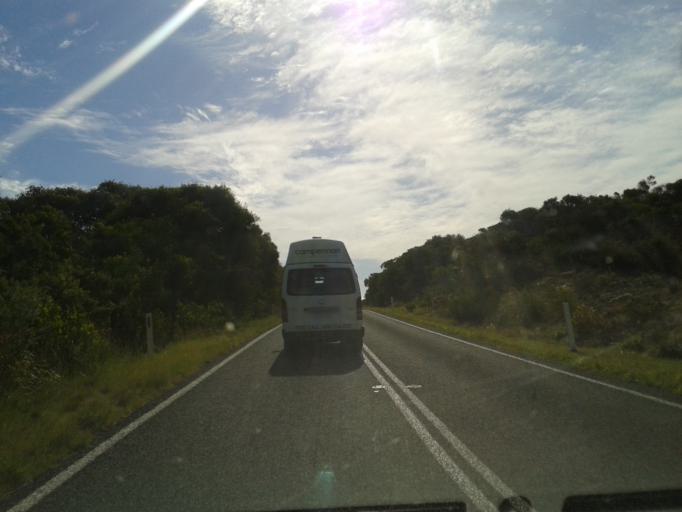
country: AU
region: Victoria
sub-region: Warrnambool
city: Allansford
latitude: -38.6398
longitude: 143.0622
